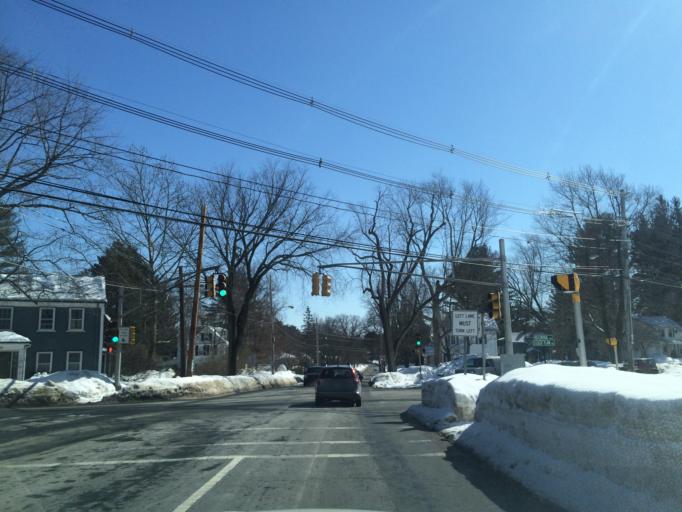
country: US
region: Massachusetts
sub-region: Norfolk County
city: Needham
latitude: 42.2838
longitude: -71.2531
